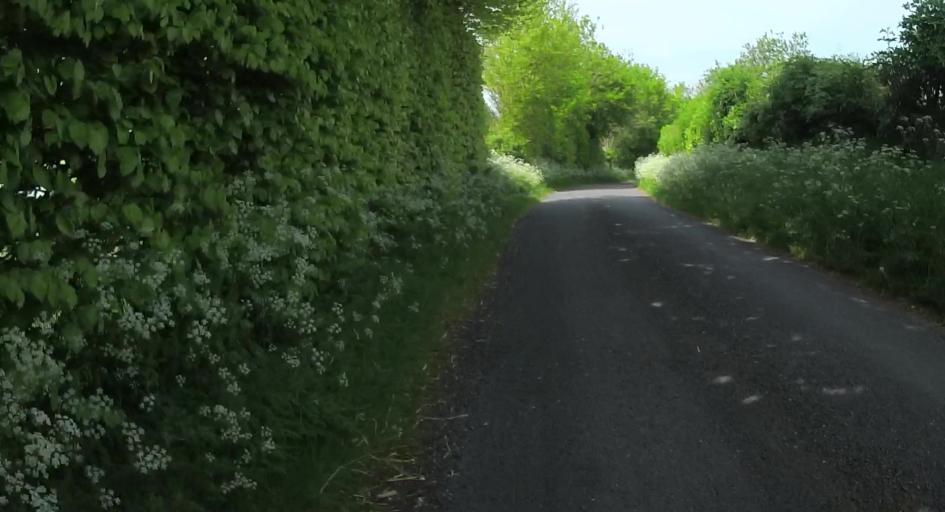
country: GB
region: England
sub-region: Hampshire
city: Kingsclere
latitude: 51.2816
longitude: -1.2329
